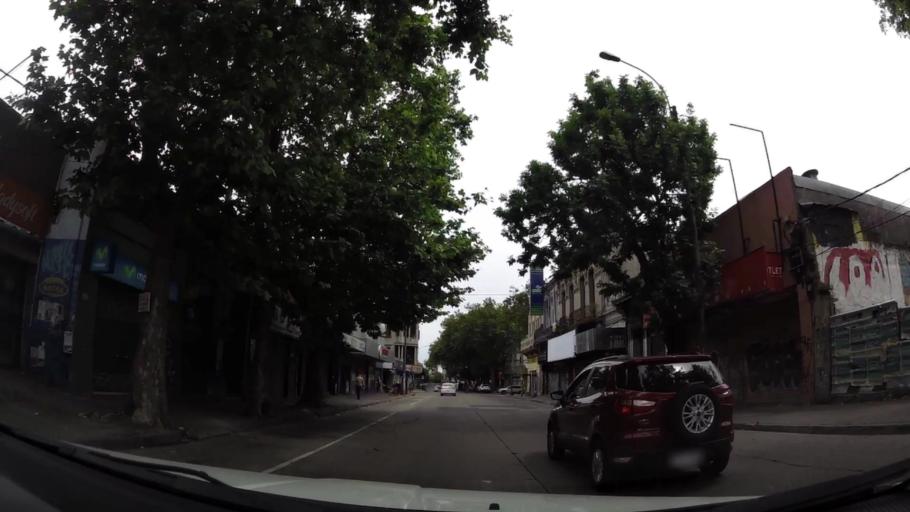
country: UY
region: Montevideo
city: Montevideo
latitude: -34.8996
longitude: -56.1765
